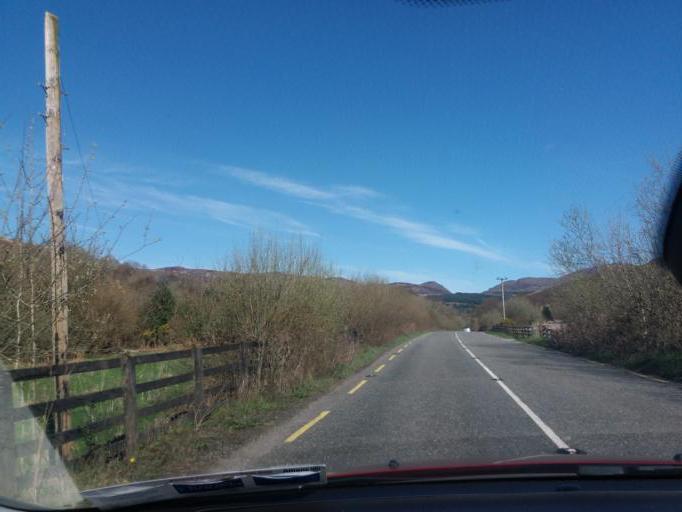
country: IE
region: Munster
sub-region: Ciarrai
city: Cill Airne
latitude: 51.9382
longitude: -9.3821
